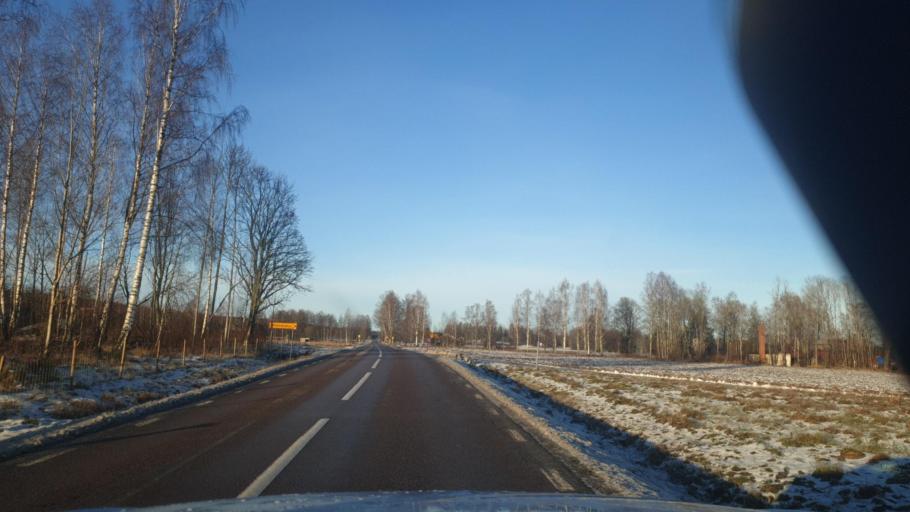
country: SE
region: Vaermland
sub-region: Arvika Kommun
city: Arvika
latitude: 59.6061
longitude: 12.5315
